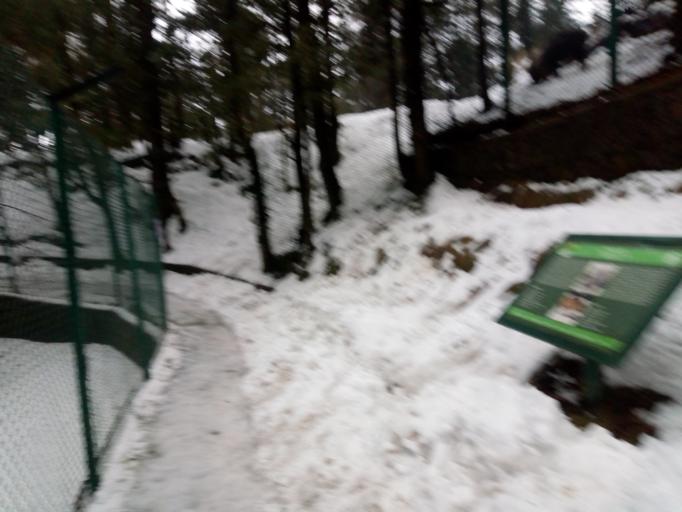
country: IN
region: Himachal Pradesh
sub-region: Shimla
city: Theog
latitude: 31.0961
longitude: 77.2645
